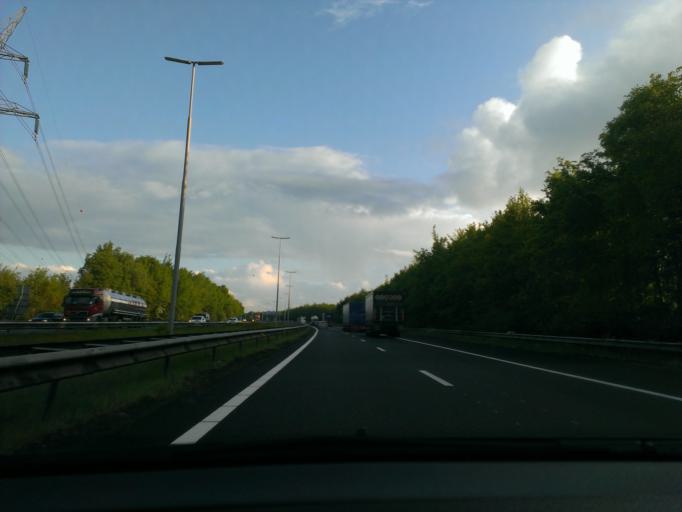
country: NL
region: Gelderland
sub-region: Gemeente Hattem
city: Hattem
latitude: 52.4743
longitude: 6.0367
